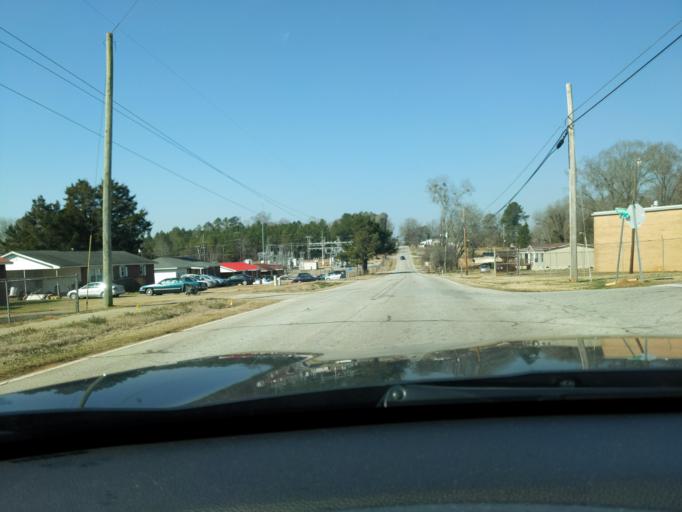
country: US
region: South Carolina
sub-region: Abbeville County
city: Calhoun Falls
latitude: 34.0872
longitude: -82.5865
